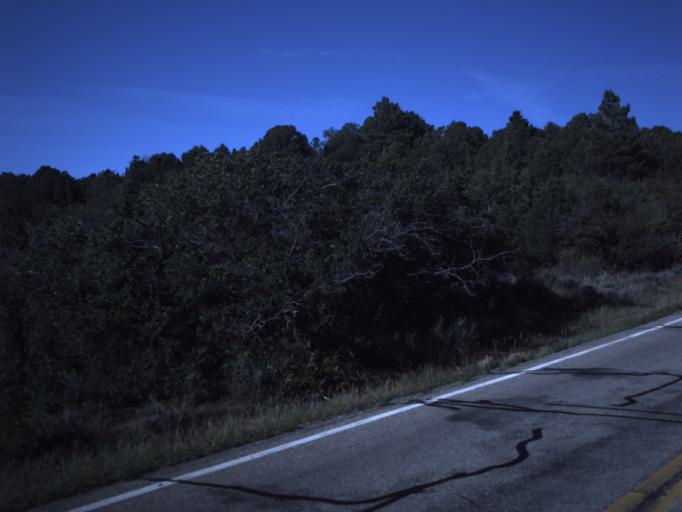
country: US
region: Utah
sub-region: Grand County
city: Moab
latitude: 38.3345
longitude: -109.2148
